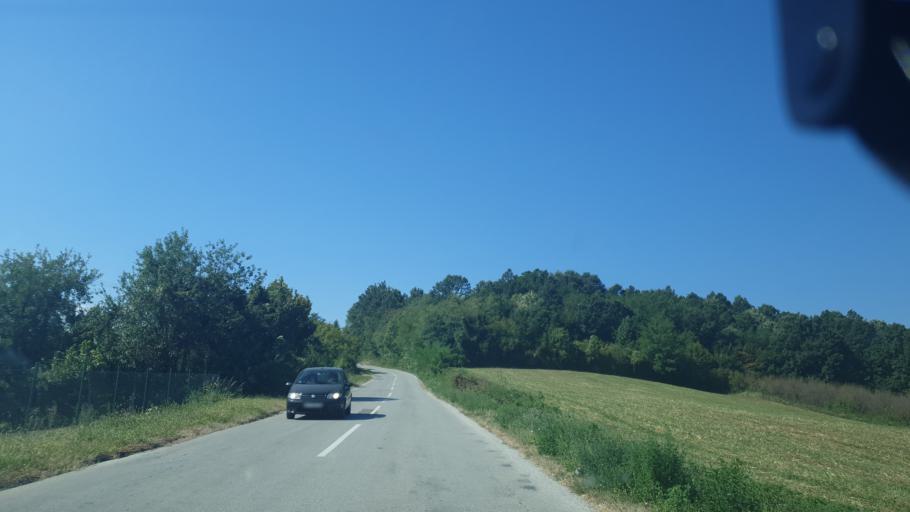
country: RS
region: Central Serbia
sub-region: Kolubarski Okrug
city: Mionica
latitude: 44.2638
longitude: 20.1043
